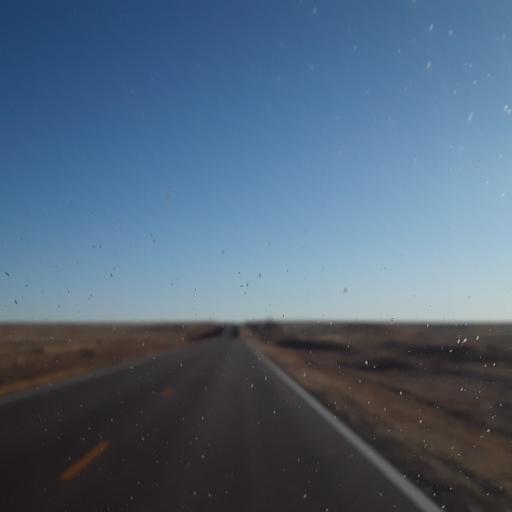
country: US
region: Kansas
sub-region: Wallace County
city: Sharon Springs
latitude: 39.0924
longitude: -101.7378
